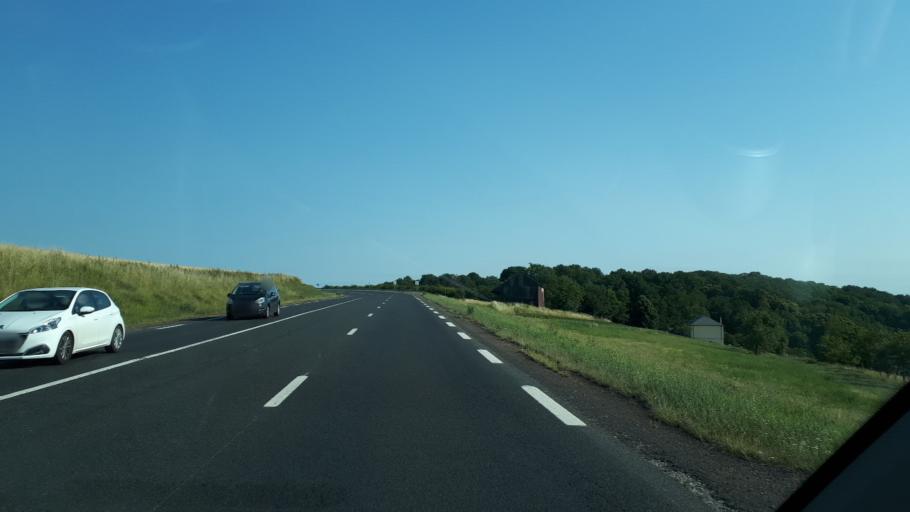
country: FR
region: Centre
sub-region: Departement du Loir-et-Cher
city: Aze
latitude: 47.8378
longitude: 0.9934
